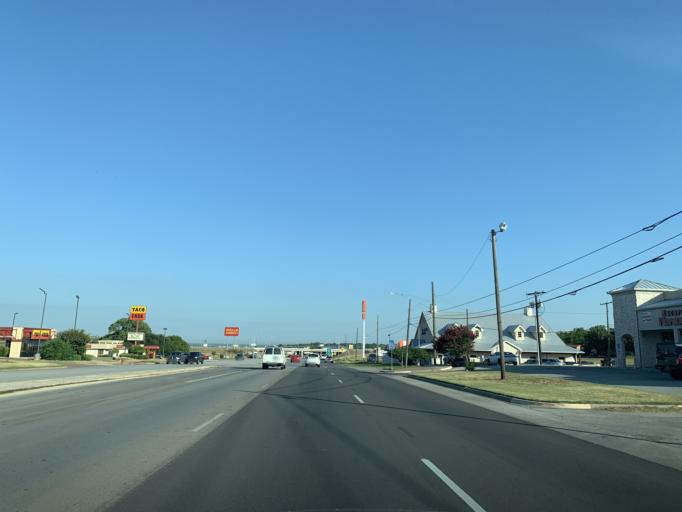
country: US
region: Texas
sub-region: Tarrant County
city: Sansom Park
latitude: 32.8061
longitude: -97.4146
